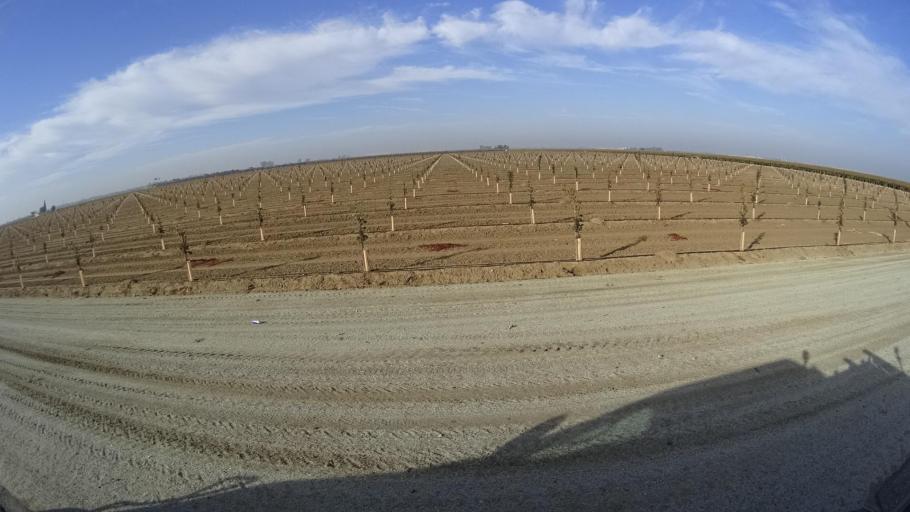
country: US
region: California
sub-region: Kern County
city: McFarland
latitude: 35.6953
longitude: -119.2049
